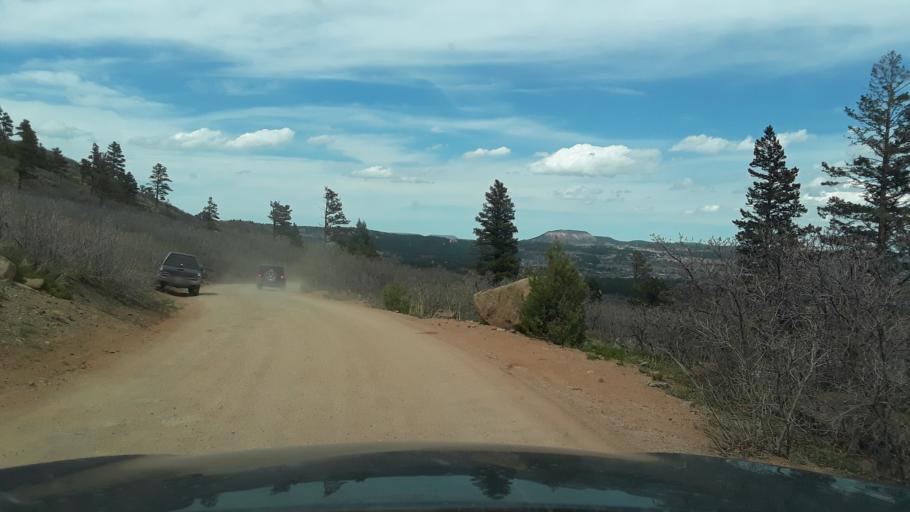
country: US
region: Colorado
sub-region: El Paso County
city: Palmer Lake
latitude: 39.0781
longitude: -104.9167
